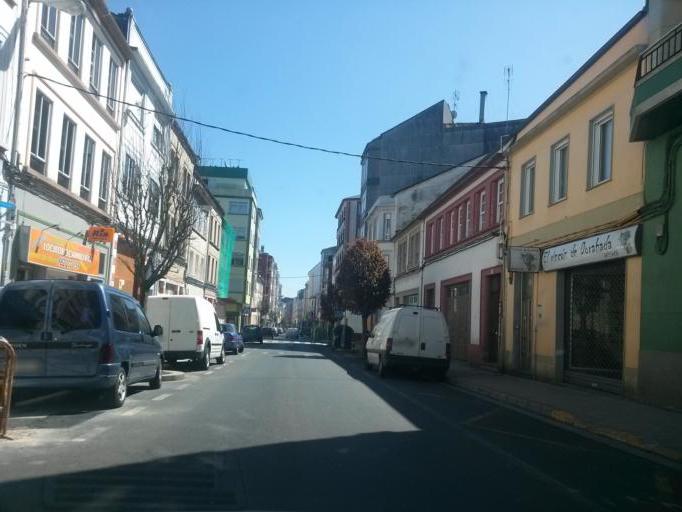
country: ES
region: Galicia
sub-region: Provincia de Lugo
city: Lugo
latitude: 43.0179
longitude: -7.5646
